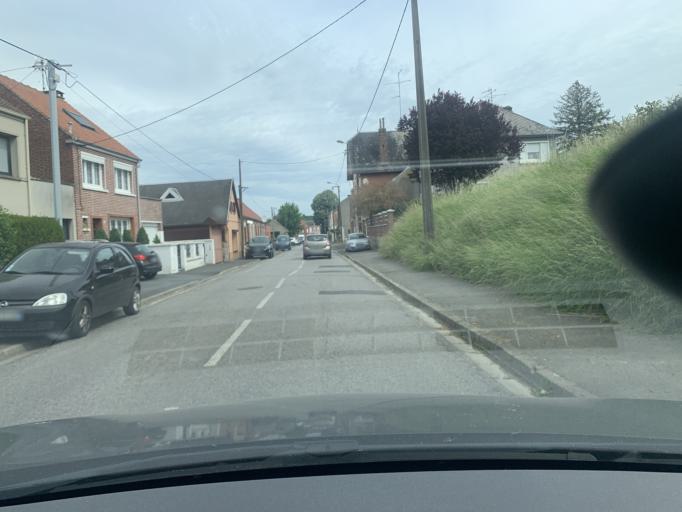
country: FR
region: Nord-Pas-de-Calais
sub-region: Departement du Nord
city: Cambrai
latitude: 50.1619
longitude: 3.2365
